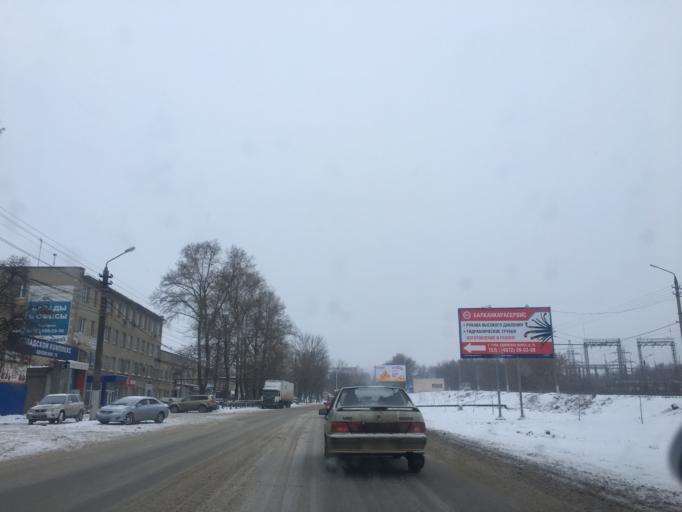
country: RU
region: Tula
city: Kosaya Gora
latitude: 54.1897
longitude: 37.5365
